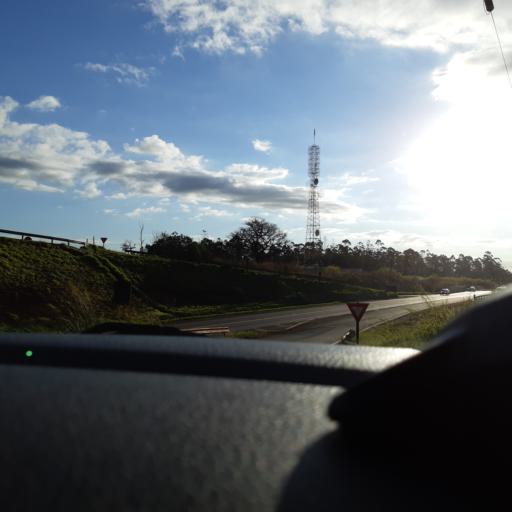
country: BR
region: Sao Paulo
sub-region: Ourinhos
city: Ourinhos
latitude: -22.9936
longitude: -49.8456
